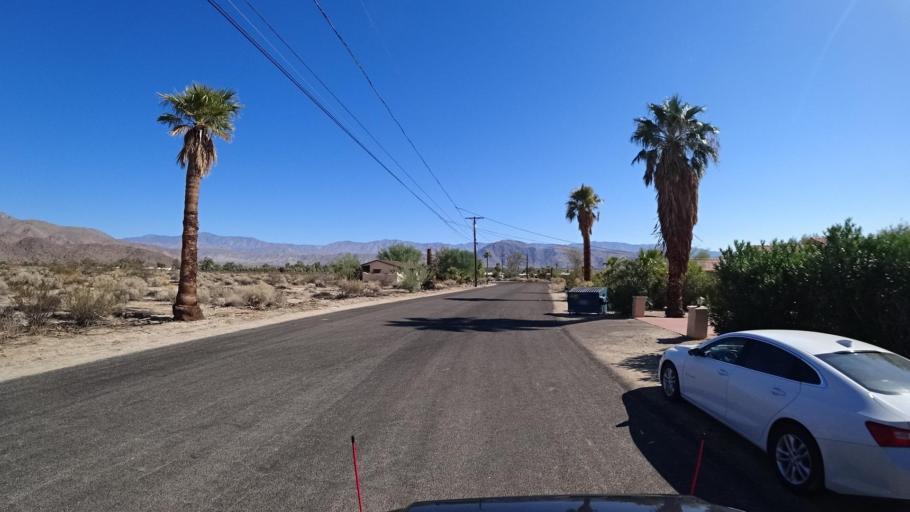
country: US
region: California
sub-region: San Diego County
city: Borrego Springs
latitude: 33.2771
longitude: -116.3940
